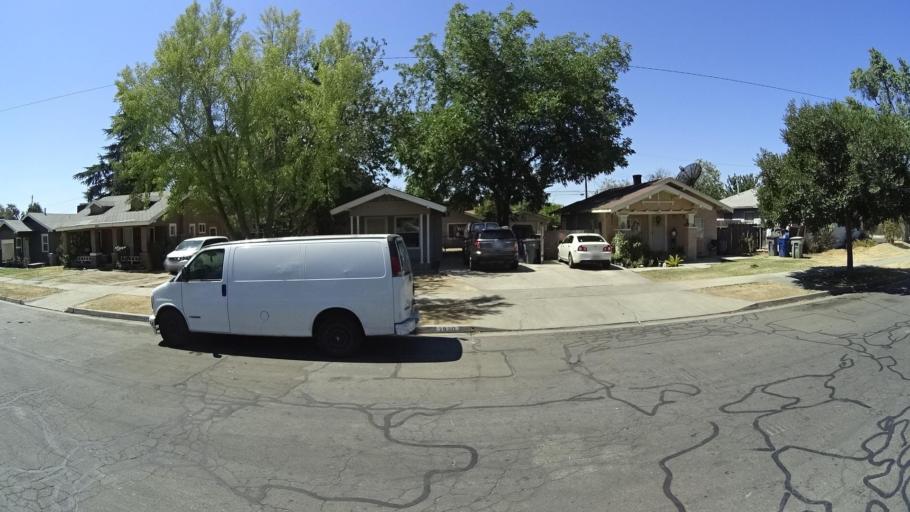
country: US
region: California
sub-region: Fresno County
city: Fresno
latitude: 36.7370
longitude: -119.7605
